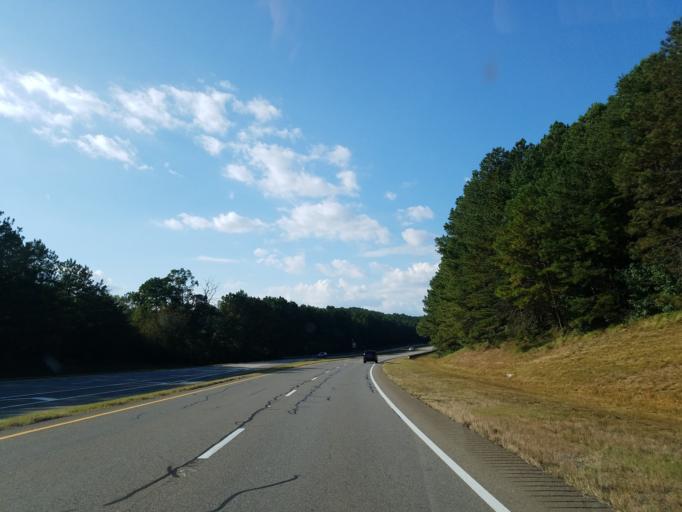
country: US
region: Georgia
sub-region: Pickens County
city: Jasper
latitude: 34.5078
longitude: -84.5160
